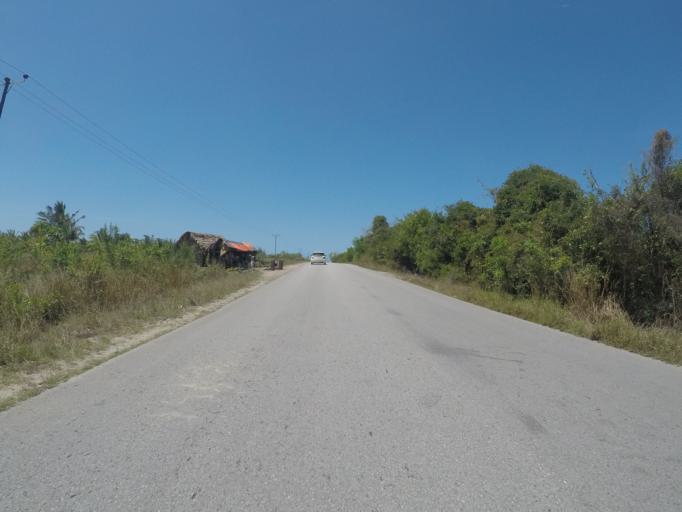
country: TZ
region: Zanzibar Central/South
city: Nganane
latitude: -6.2746
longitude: 39.4891
